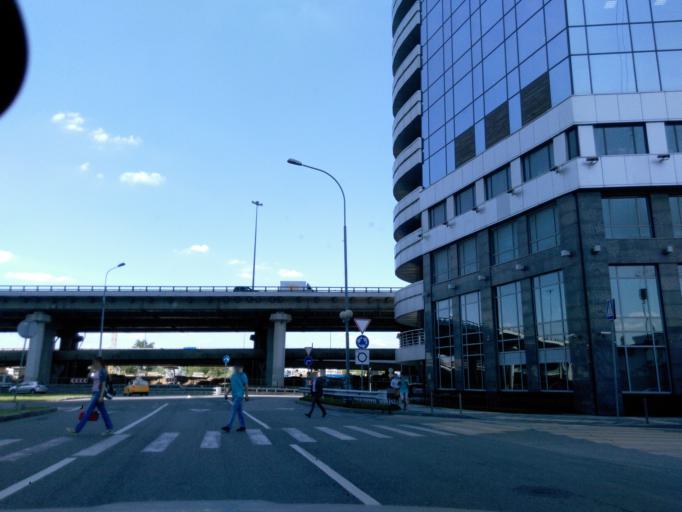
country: RU
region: Moskovskaya
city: Presnenskiy
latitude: 55.7503
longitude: 37.5335
